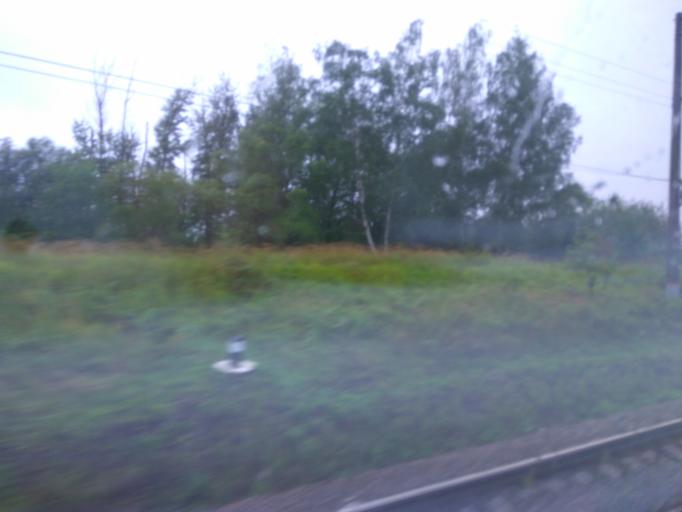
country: RU
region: Moskovskaya
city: Stupino
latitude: 54.9016
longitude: 38.0859
